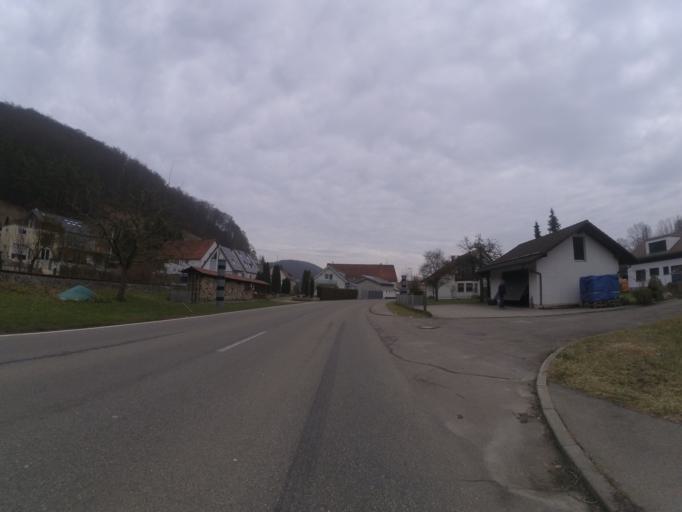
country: DE
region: Baden-Wuerttemberg
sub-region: Tuebingen Region
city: Schelklingen
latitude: 48.3655
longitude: 9.7134
